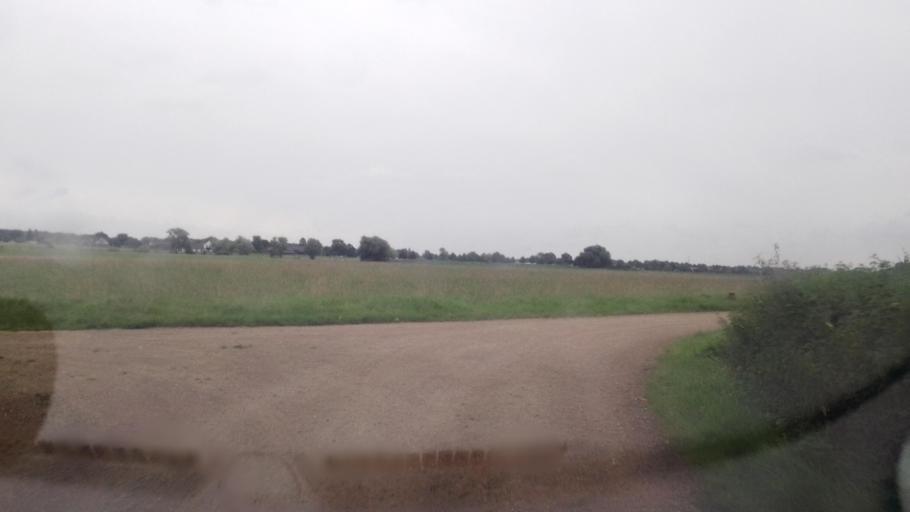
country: NL
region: Limburg
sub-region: Gemeente Venlo
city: Arcen
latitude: 51.4265
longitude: 6.1518
